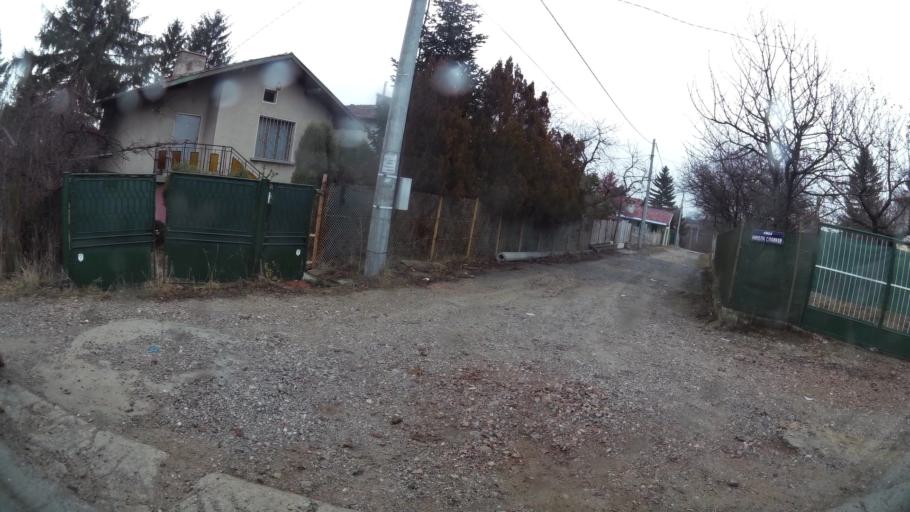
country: BG
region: Sofia-Capital
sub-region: Stolichna Obshtina
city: Sofia
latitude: 42.5996
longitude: 23.3886
